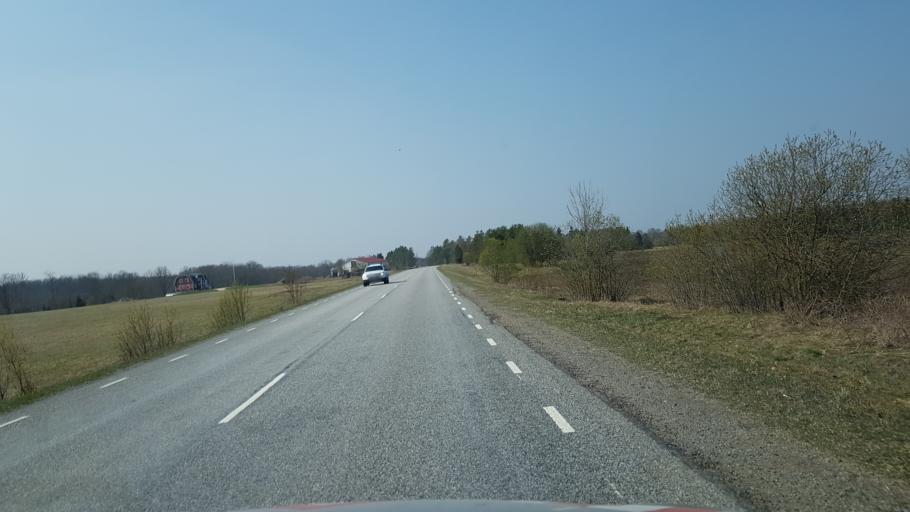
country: EE
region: Harju
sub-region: Paldiski linn
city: Paldiski
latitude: 59.2389
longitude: 23.9407
